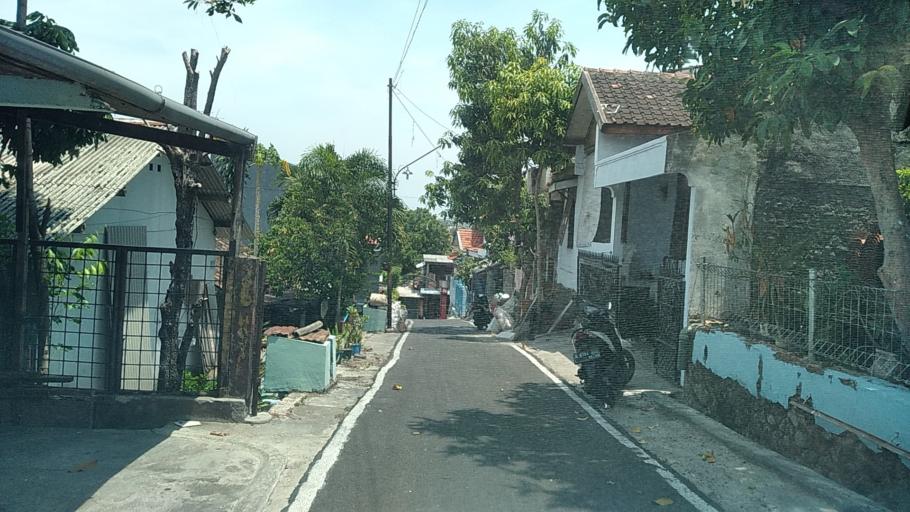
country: ID
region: Central Java
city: Semarang
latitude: -7.0111
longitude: 110.4482
